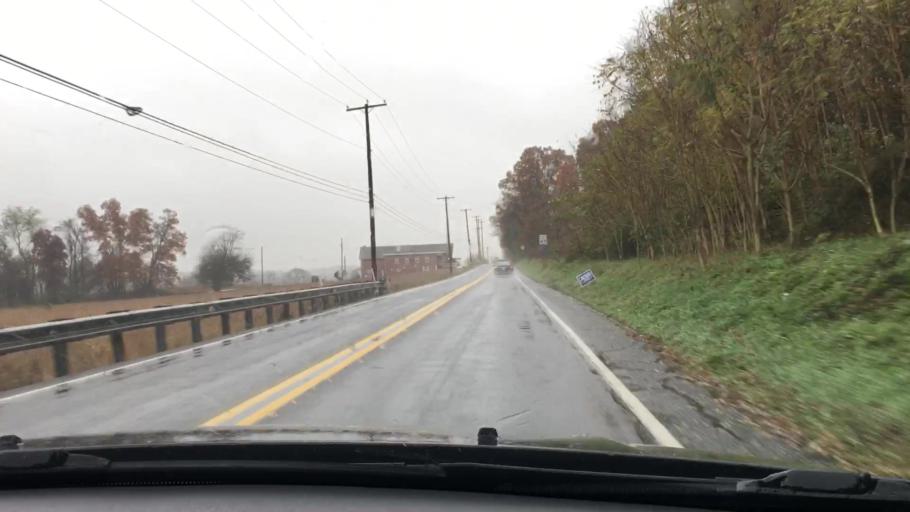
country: US
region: Pennsylvania
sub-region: York County
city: Glen Rock
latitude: 39.7507
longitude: -76.7900
